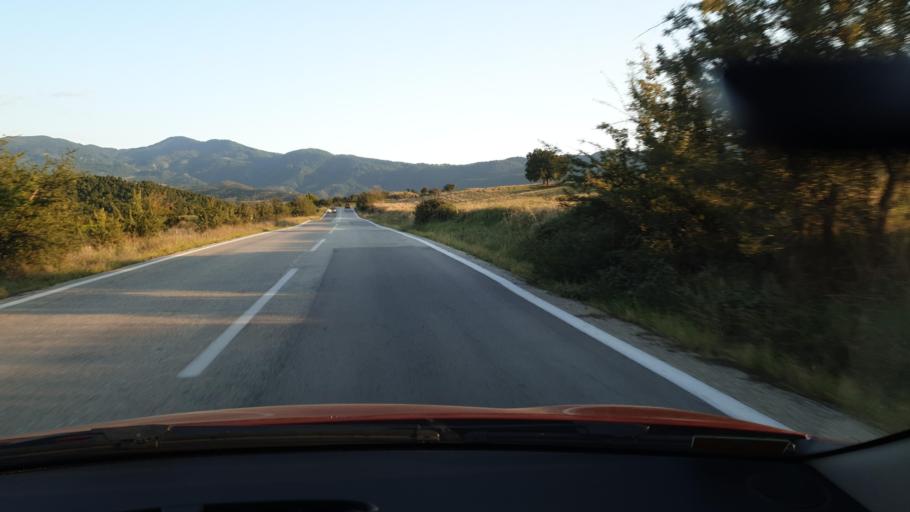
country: GR
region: Central Macedonia
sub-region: Nomos Thessalonikis
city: Nea Apollonia
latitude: 40.5220
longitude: 23.4717
